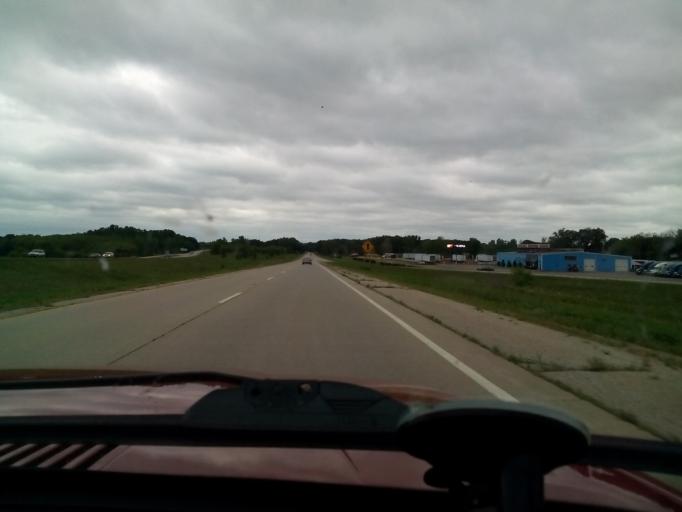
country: US
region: Wisconsin
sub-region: Dane County
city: Sun Prairie
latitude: 43.2402
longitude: -89.1478
